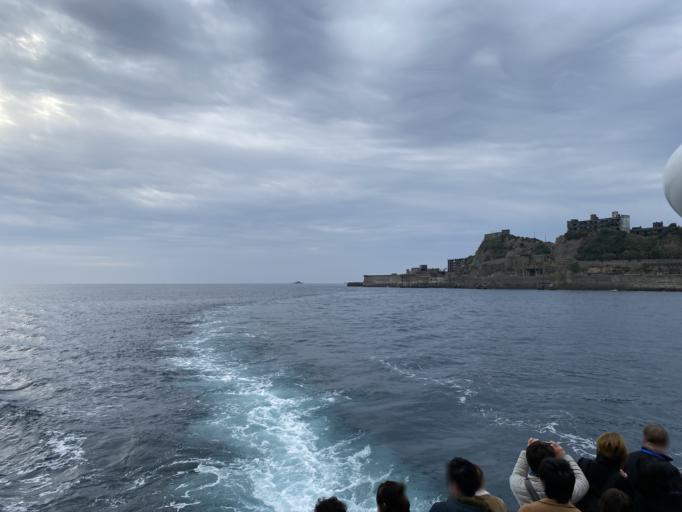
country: JP
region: Nagasaki
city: Nagasaki-shi
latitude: 32.6278
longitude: 129.7426
